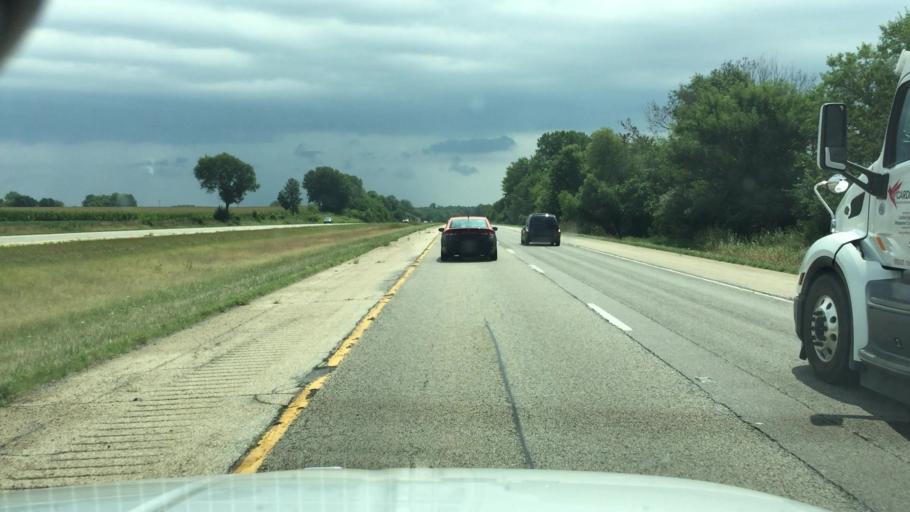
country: US
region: Illinois
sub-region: Peoria County
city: Elmwood
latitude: 40.8149
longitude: -89.8474
